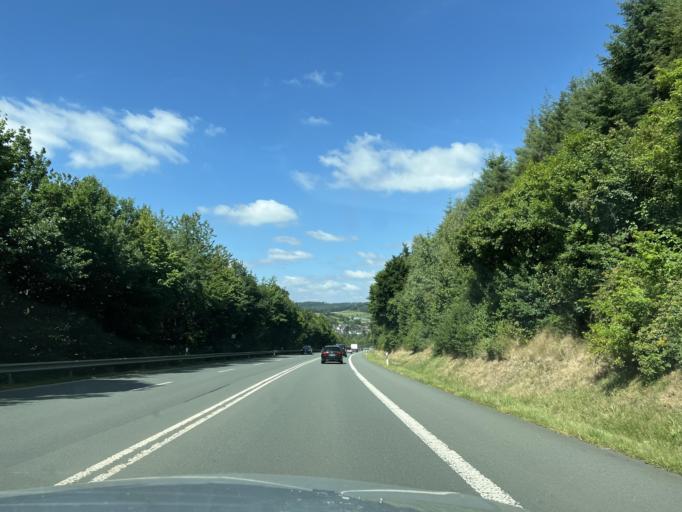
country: DE
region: North Rhine-Westphalia
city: Freudenberg
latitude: 50.9102
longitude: 7.9042
